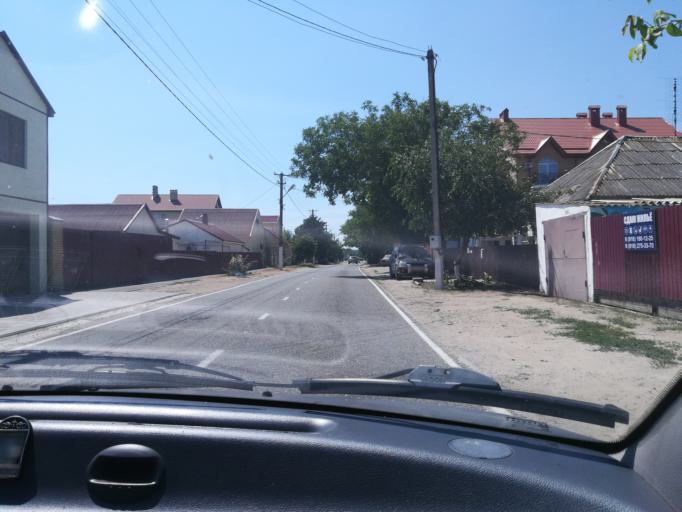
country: RU
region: Krasnodarskiy
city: Blagovetschenskaya
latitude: 45.0555
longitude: 37.1349
